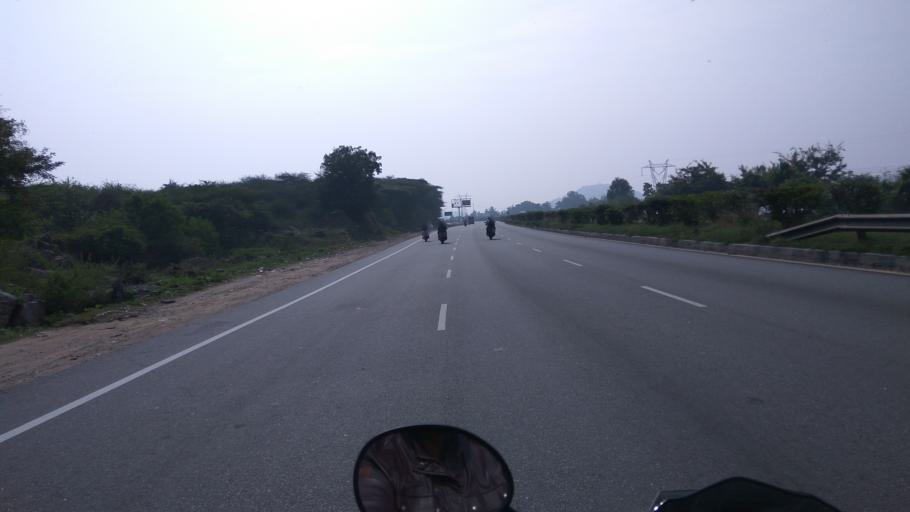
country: IN
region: Tamil Nadu
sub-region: Krishnagiri
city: Krishnagiri
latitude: 12.6126
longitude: 78.0905
